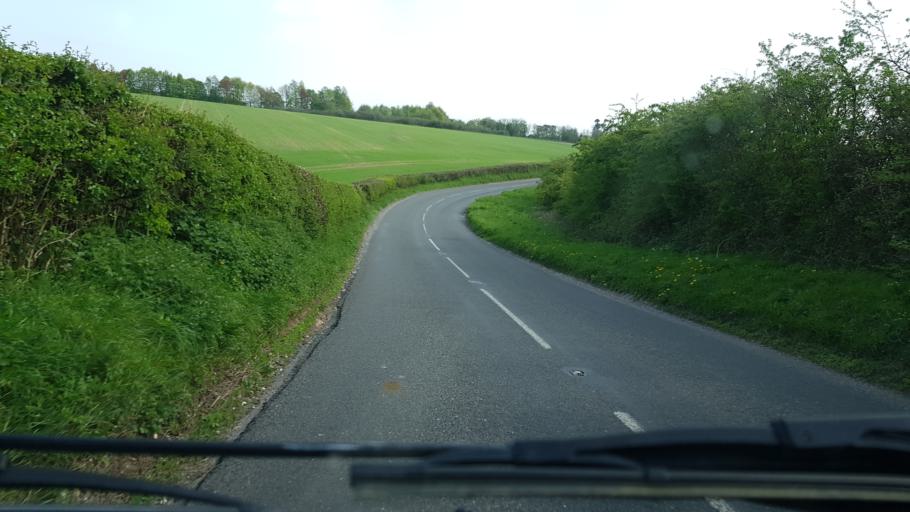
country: GB
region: England
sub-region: Hampshire
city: Overton
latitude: 51.2586
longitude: -1.2638
